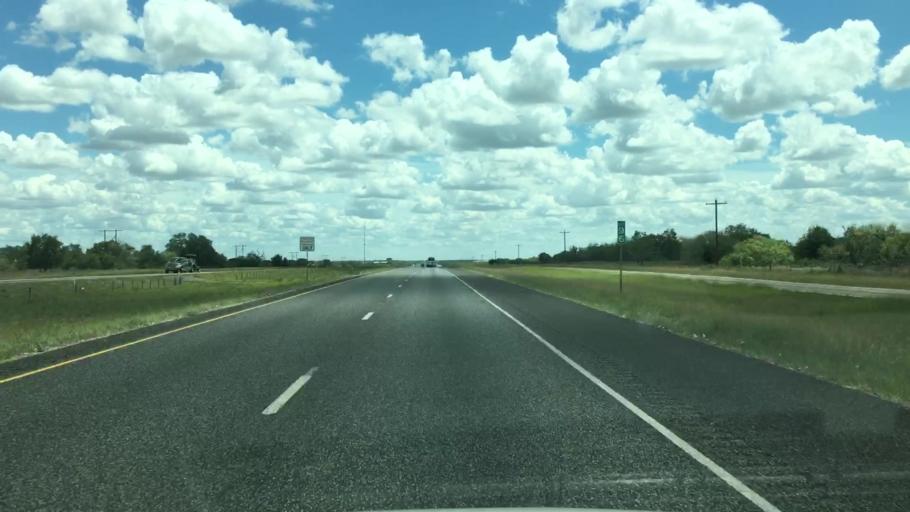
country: US
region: Texas
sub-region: Atascosa County
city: Pleasanton
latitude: 28.8169
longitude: -98.3582
